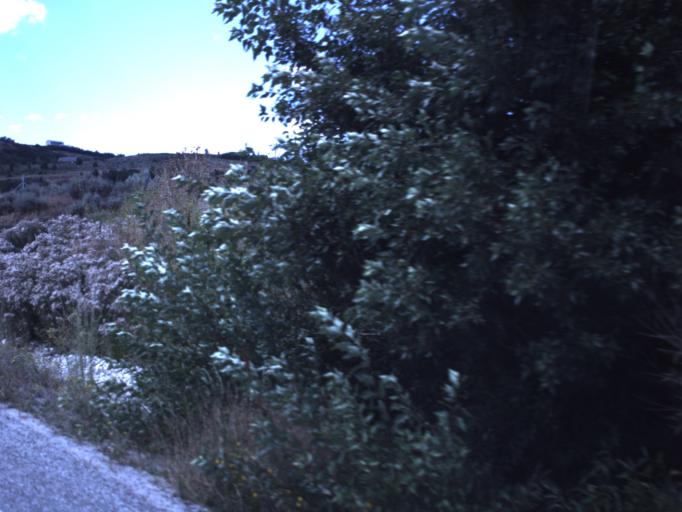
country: US
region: Idaho
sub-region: Bear Lake County
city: Paris
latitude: 41.9309
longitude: -111.4224
